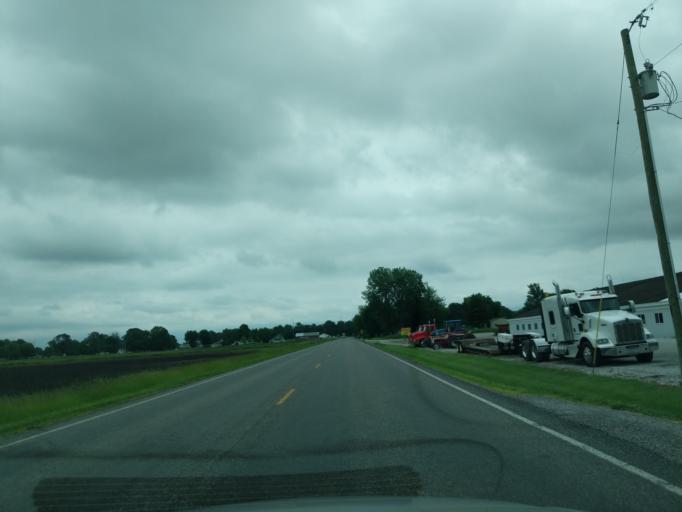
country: US
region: Indiana
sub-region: Tipton County
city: Tipton
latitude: 40.2852
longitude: -85.9531
